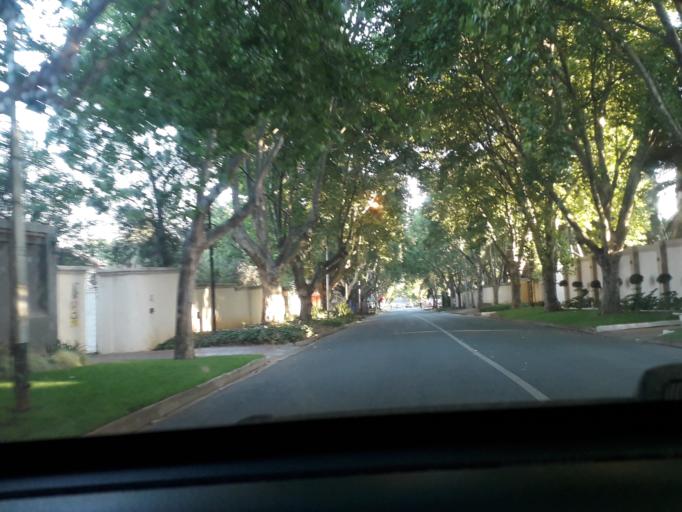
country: ZA
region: Gauteng
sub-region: City of Johannesburg Metropolitan Municipality
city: Johannesburg
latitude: -26.1575
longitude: 28.0536
